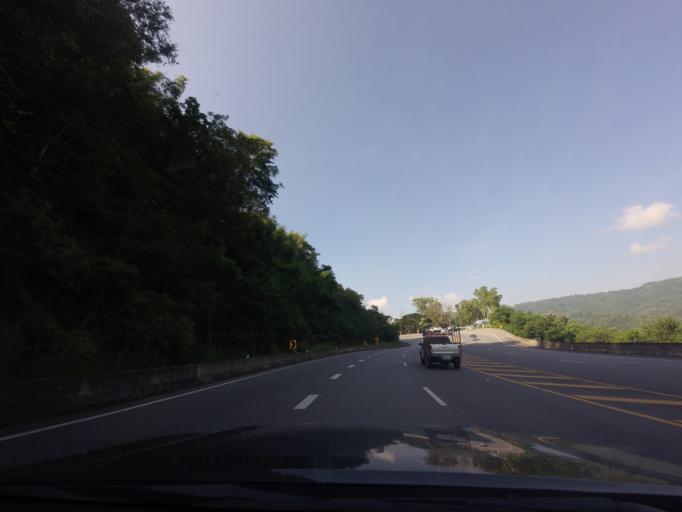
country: TH
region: Phetchabun
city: Khao Kho
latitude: 16.7836
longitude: 101.0856
